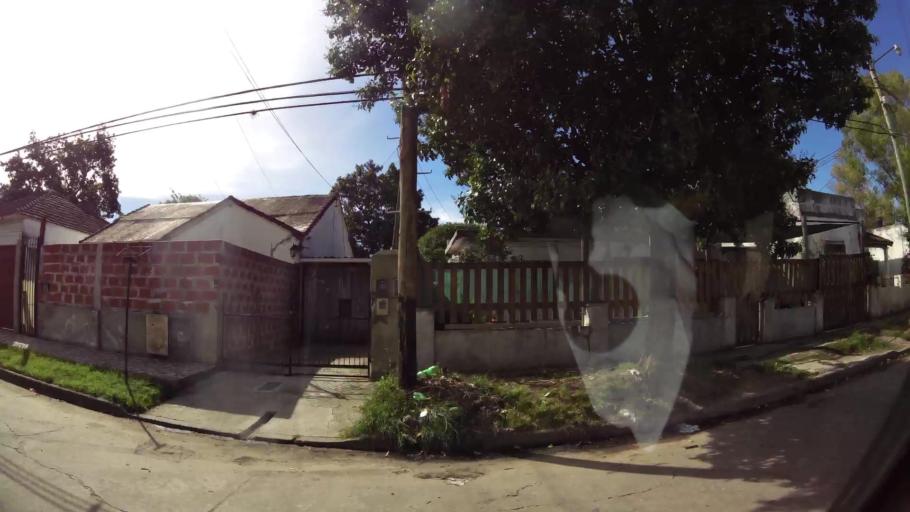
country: AR
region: Buenos Aires
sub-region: Partido de Almirante Brown
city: Adrogue
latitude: -34.8012
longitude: -58.3546
